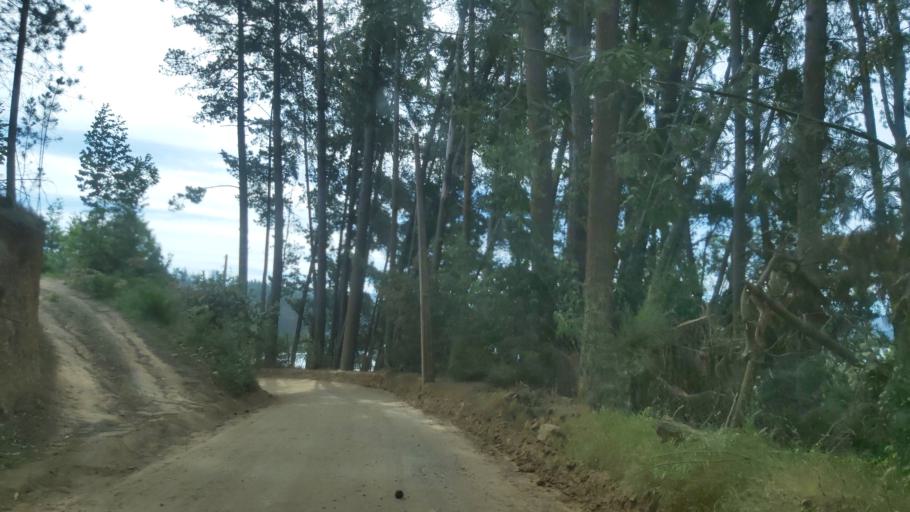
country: CL
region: Maule
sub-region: Provincia de Talca
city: Constitucion
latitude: -34.8457
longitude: -72.0399
